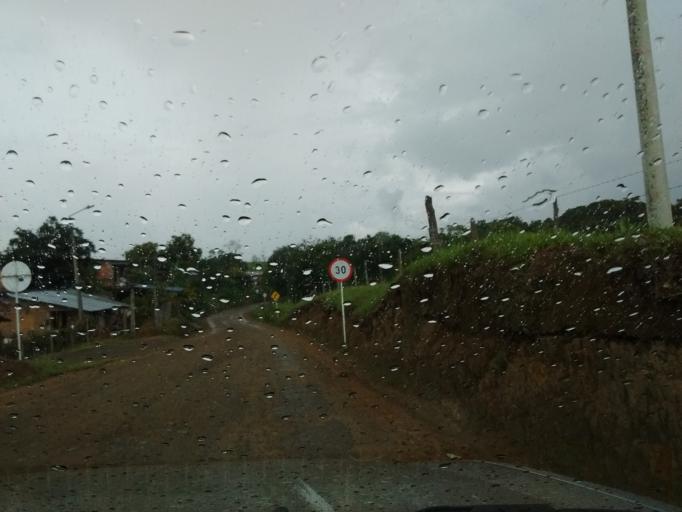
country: CO
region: Cauca
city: Popayan
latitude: 2.5199
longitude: -76.5921
